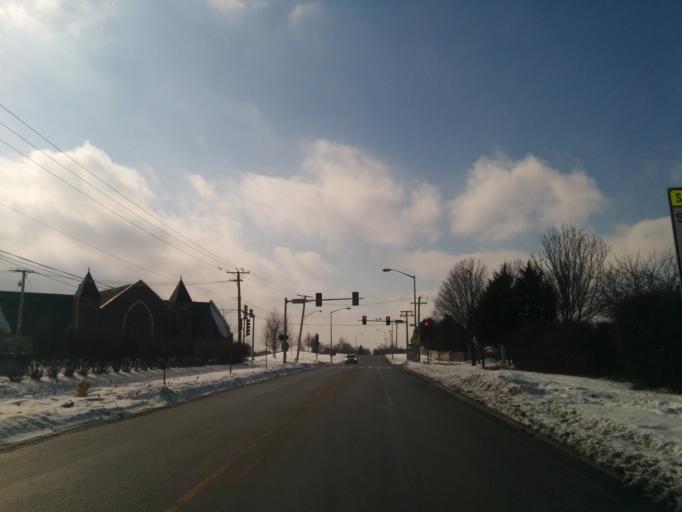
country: US
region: Illinois
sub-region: Cook County
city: Orland Hills
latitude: 41.5728
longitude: -87.8216
